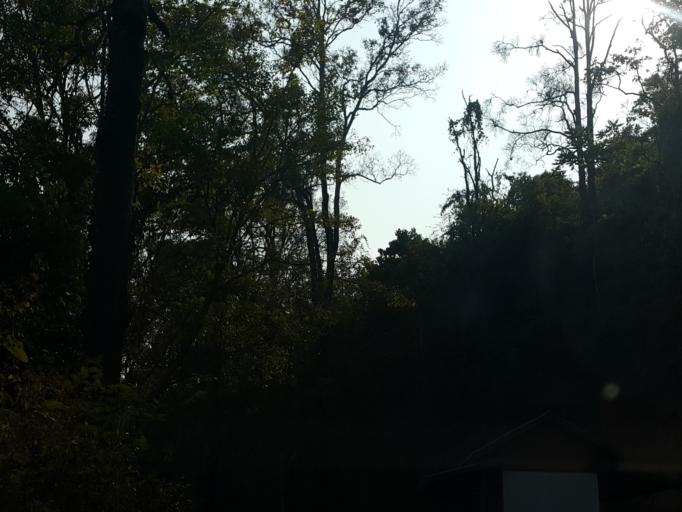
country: TH
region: Chiang Mai
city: Samoeng
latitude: 19.0187
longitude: 98.7632
